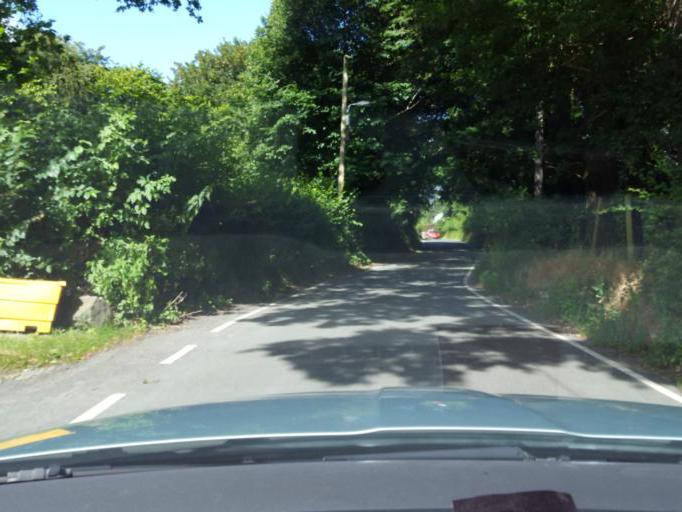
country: GB
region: Wales
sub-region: Denbighshire
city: Corwen
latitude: 52.9820
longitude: -3.3281
